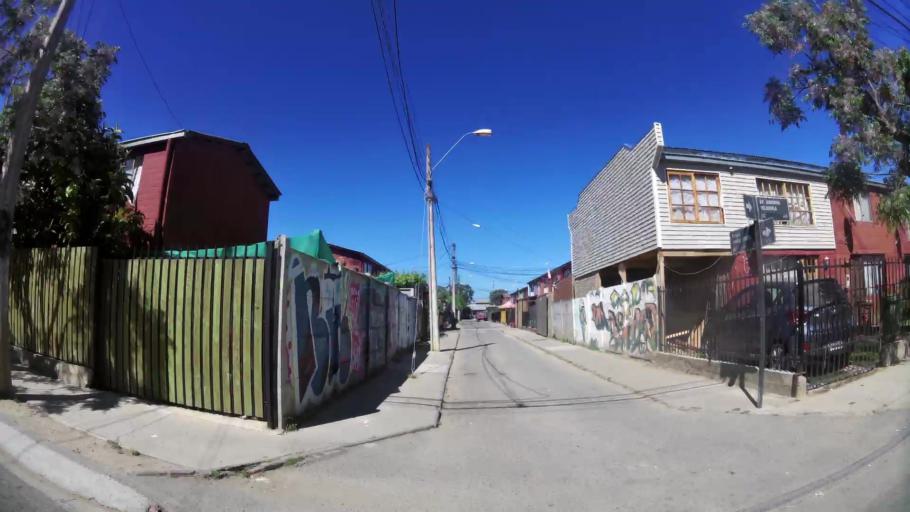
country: CL
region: Valparaiso
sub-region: Provincia de Marga Marga
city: Quilpue
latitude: -33.3069
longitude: -71.4120
